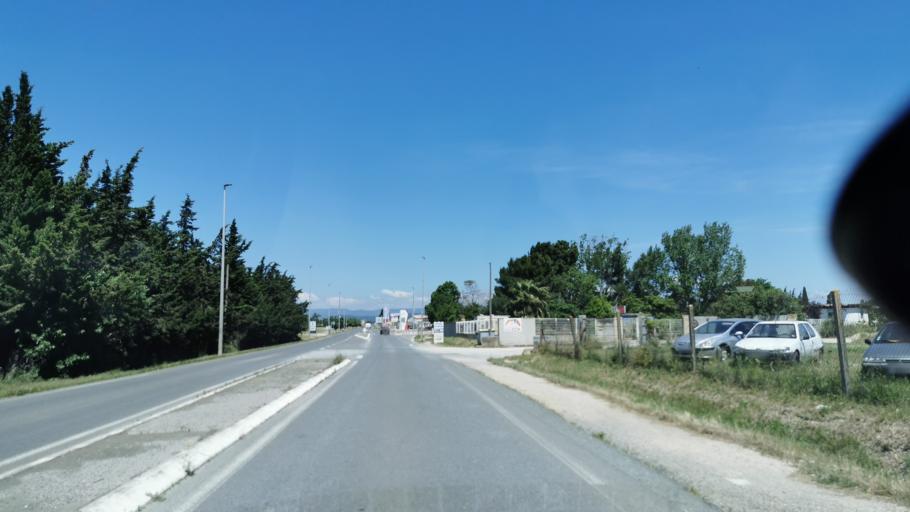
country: FR
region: Languedoc-Roussillon
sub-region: Departement de l'Aude
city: Saint-Marcel-sur-Aude
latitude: 43.2523
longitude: 2.9141
